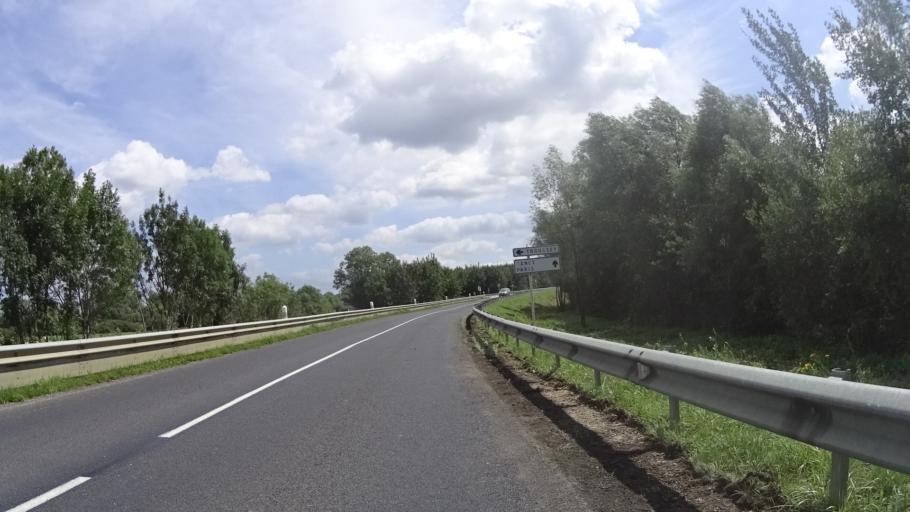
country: FR
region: Lorraine
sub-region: Departement de la Meuse
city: Euville
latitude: 48.7111
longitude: 5.6788
